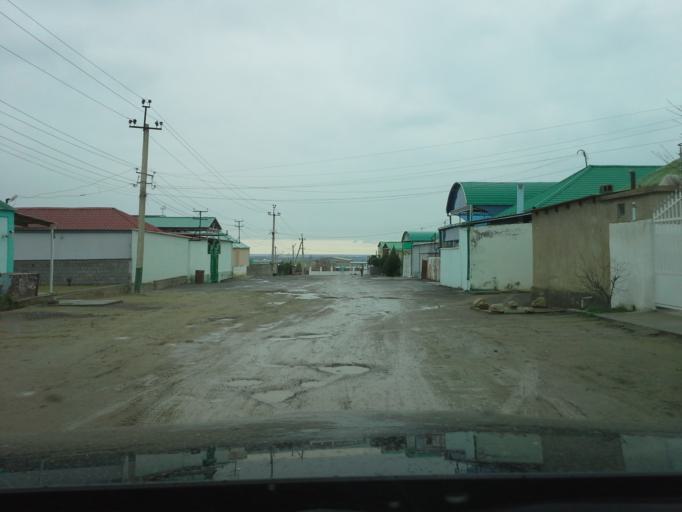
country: TM
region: Ahal
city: Abadan
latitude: 37.9588
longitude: 58.2023
